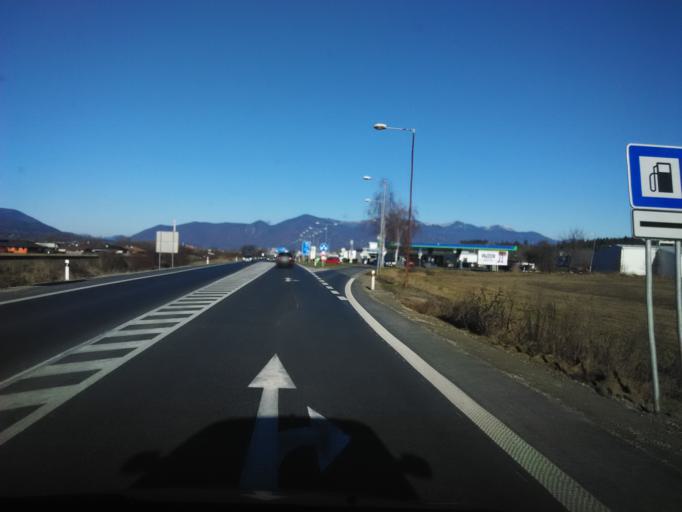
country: SK
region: Zilinsky
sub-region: Okres Martin
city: Martin
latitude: 49.0322
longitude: 18.9072
